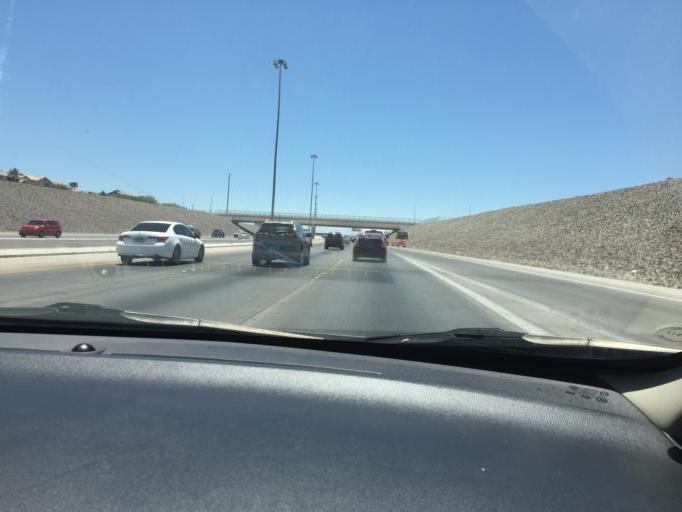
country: US
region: Nevada
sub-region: Clark County
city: Whitney
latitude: 36.0377
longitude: -115.1338
